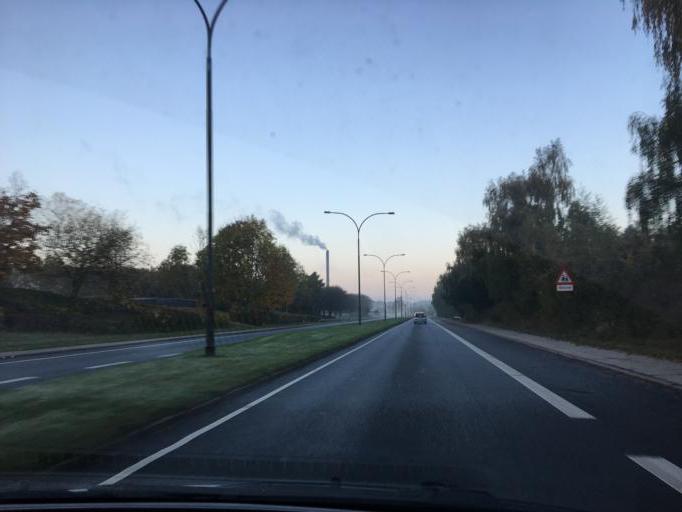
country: DK
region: South Denmark
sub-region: Vejle Kommune
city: Vejle
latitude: 55.6726
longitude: 9.5358
